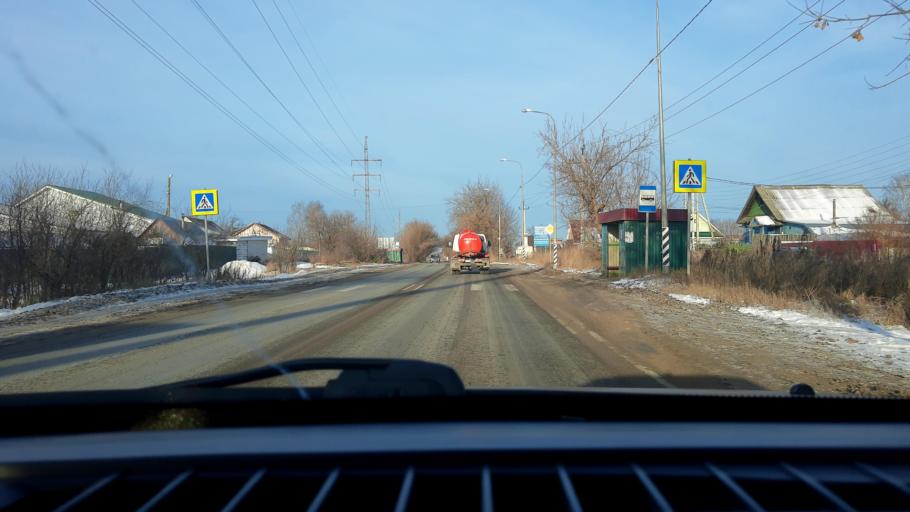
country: RU
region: Nizjnij Novgorod
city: Bor
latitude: 56.3654
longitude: 44.0716
